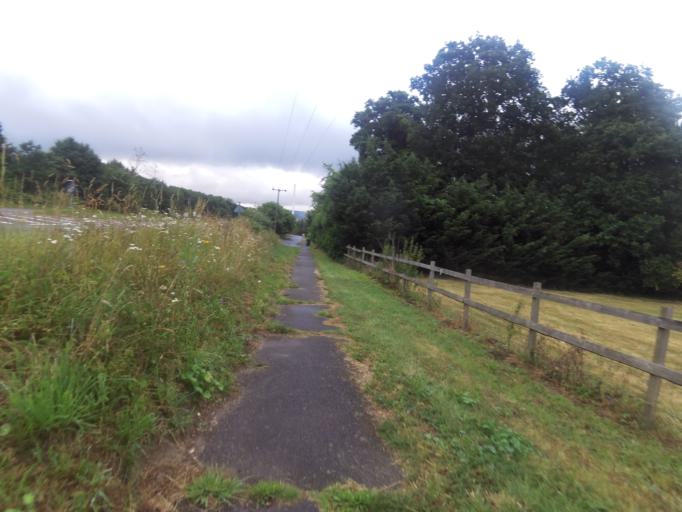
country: GB
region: England
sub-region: Suffolk
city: Bramford
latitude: 52.0992
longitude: 1.0953
